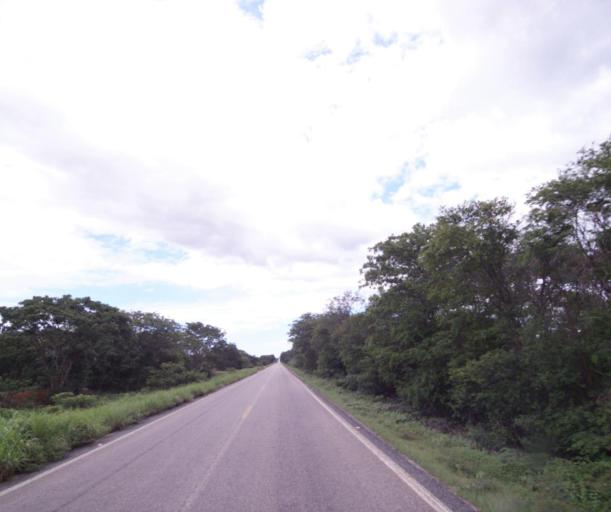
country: BR
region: Bahia
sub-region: Palmas De Monte Alto
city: Palmas de Monte Alto
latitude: -14.2611
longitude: -43.3048
